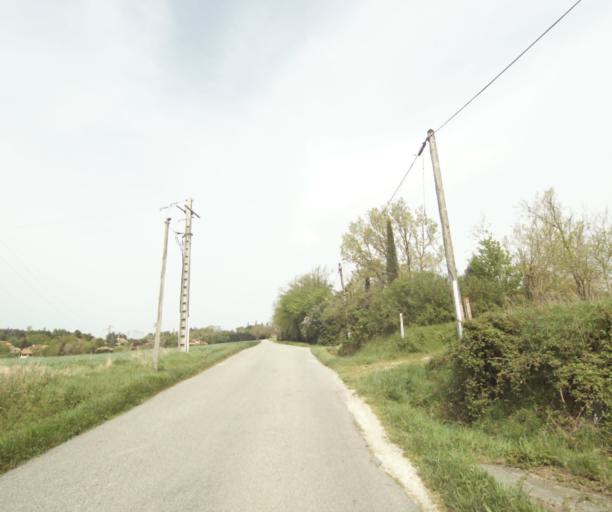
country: FR
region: Midi-Pyrenees
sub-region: Departement de la Haute-Garonne
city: Pompertuzat
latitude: 43.4854
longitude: 1.5020
